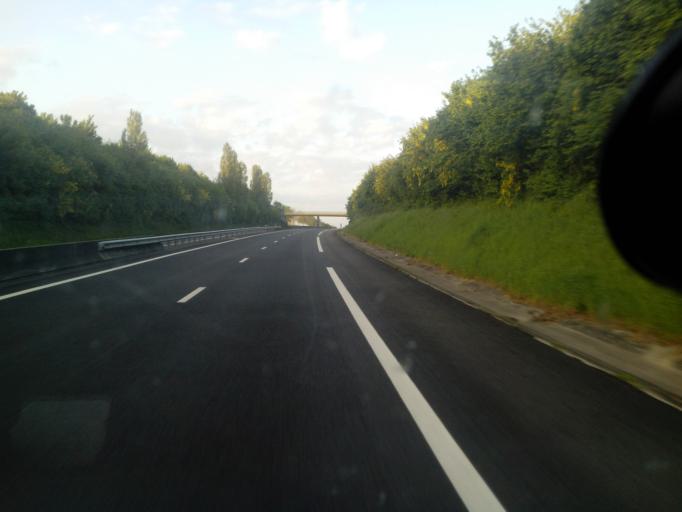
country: FR
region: Picardie
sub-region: Departement de la Somme
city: Chepy
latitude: 50.0079
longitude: 1.6971
